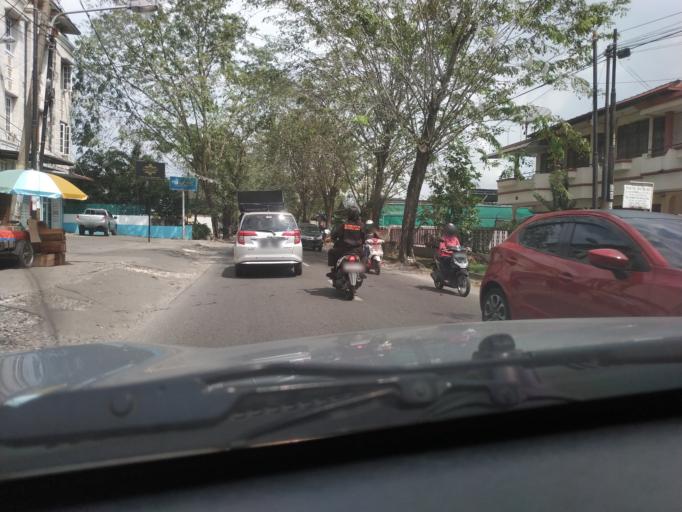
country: ID
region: North Sumatra
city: Sunggal
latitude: 3.5845
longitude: 98.6339
